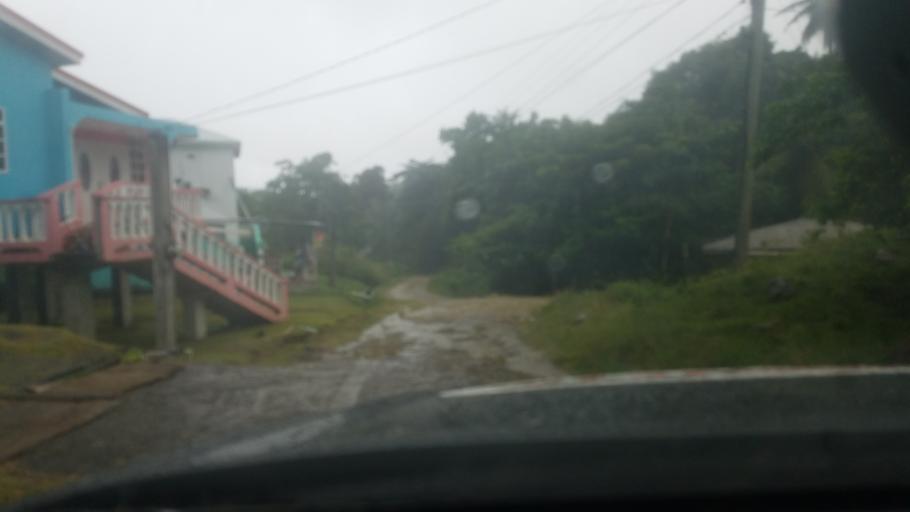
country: LC
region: Gros-Islet
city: Gros Islet
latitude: 14.0454
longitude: -60.9388
